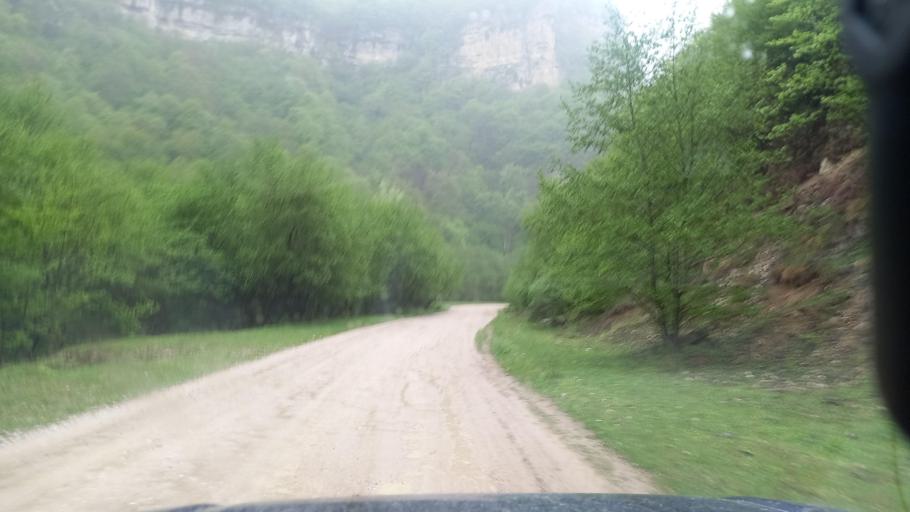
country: RU
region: Kabardino-Balkariya
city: Gundelen
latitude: 43.5921
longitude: 43.1304
